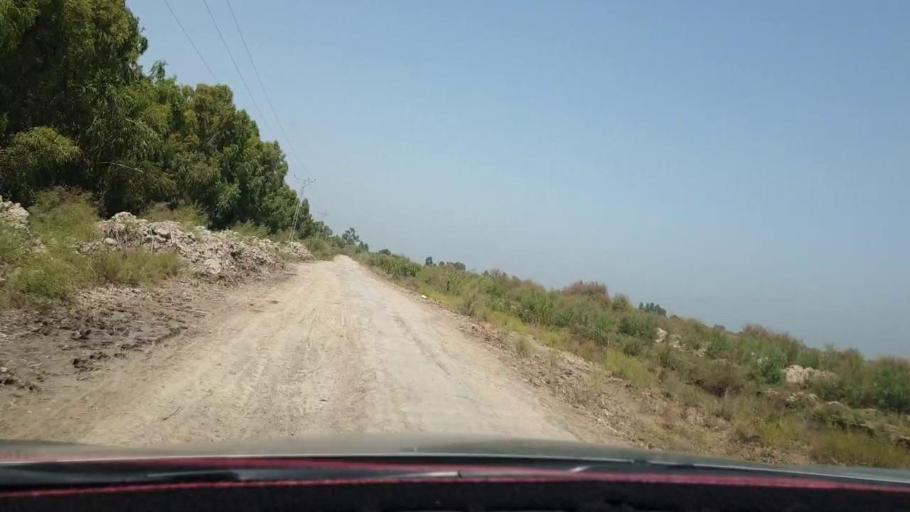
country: PK
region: Sindh
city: Warah
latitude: 27.4249
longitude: 67.6986
